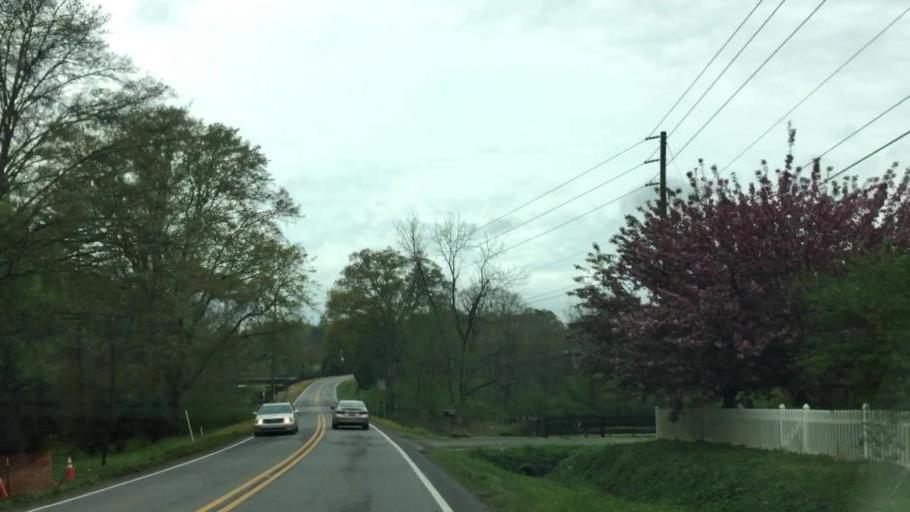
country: US
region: Georgia
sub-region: Cherokee County
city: Canton
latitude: 34.2214
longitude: -84.4046
